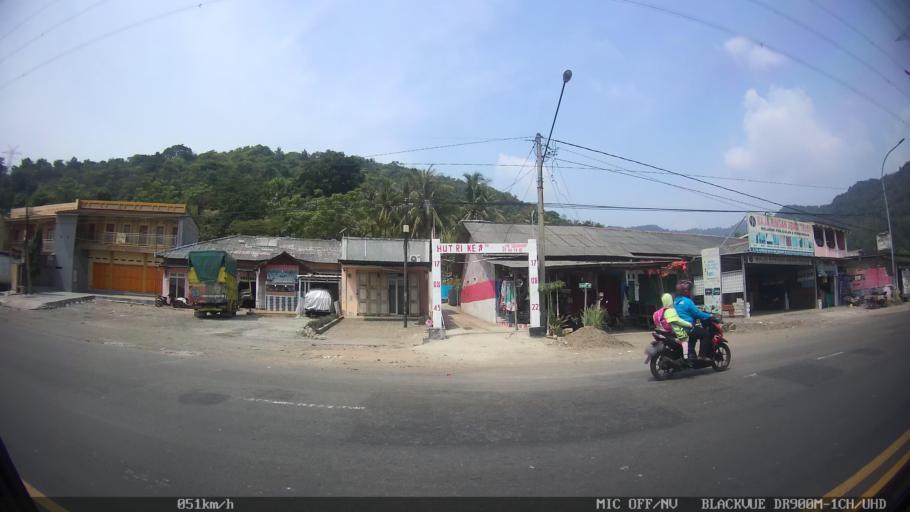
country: ID
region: Banten
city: Curug
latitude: -5.9410
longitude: 106.0051
